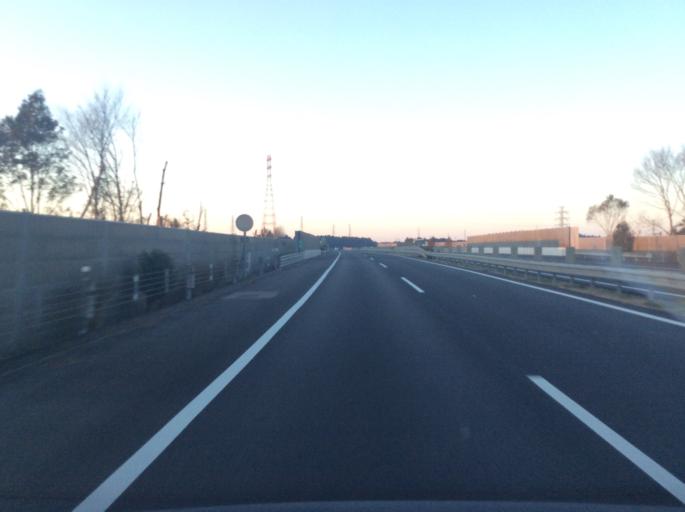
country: JP
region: Ibaraki
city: Funaishikawa
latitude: 36.4983
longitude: 140.5657
